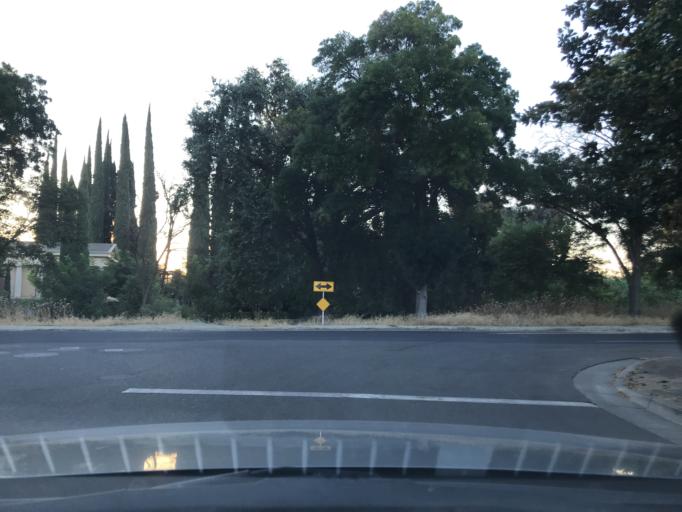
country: US
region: California
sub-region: Merced County
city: Merced
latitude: 37.3106
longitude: -120.4991
